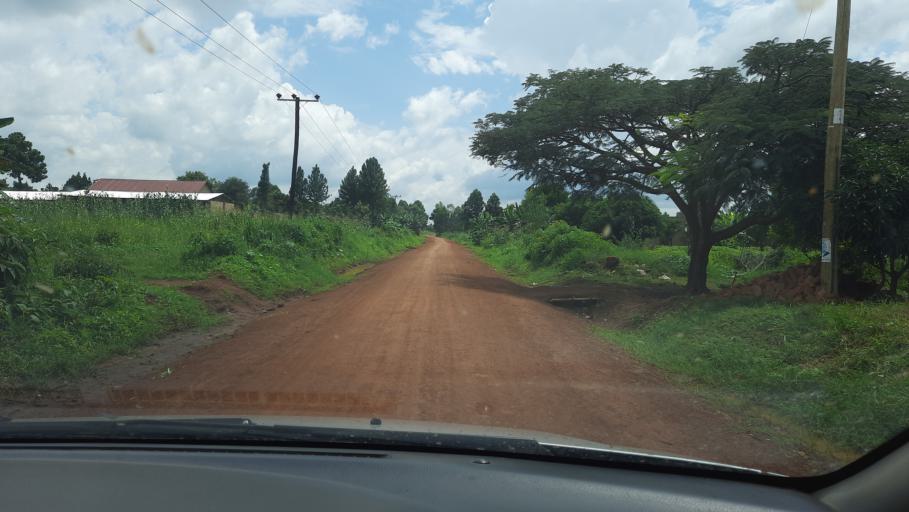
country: UG
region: Western Region
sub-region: Kiryandongo District
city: Kiryandongo
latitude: 1.8130
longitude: 31.9977
